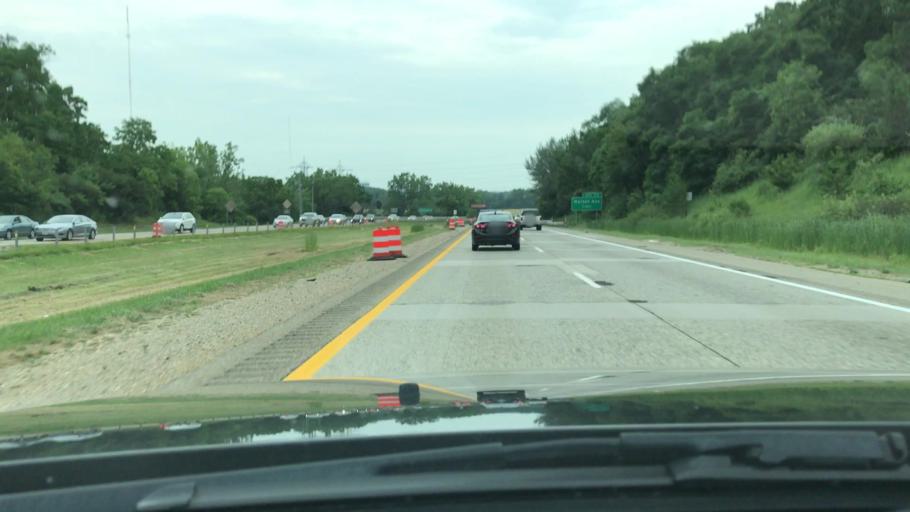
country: US
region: Michigan
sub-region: Kent County
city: Grand Rapids
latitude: 42.9588
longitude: -85.7072
